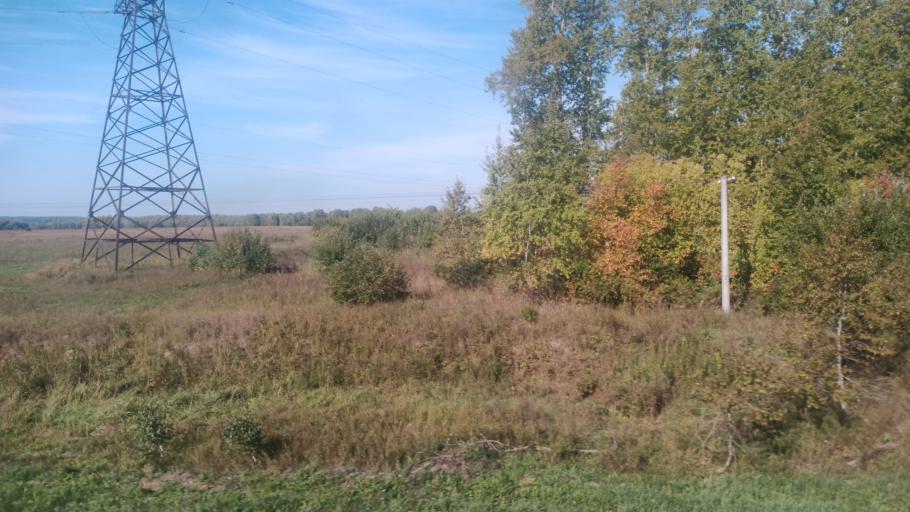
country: RU
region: Altai Krai
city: Troitskoye
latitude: 53.1004
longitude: 84.6751
